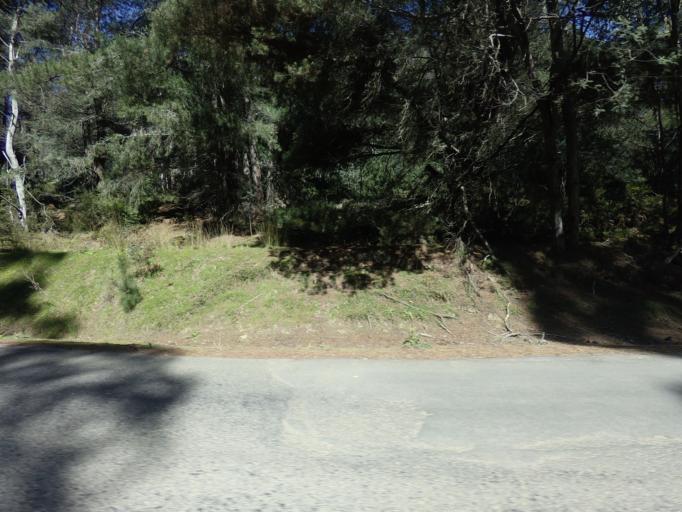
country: AU
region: Tasmania
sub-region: Derwent Valley
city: New Norfolk
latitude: -42.7624
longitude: 146.6037
